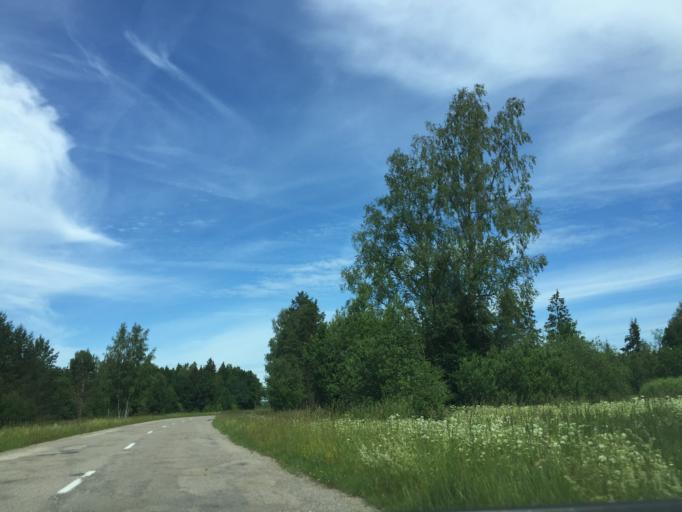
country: LV
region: Dundaga
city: Dundaga
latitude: 57.5946
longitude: 22.2927
